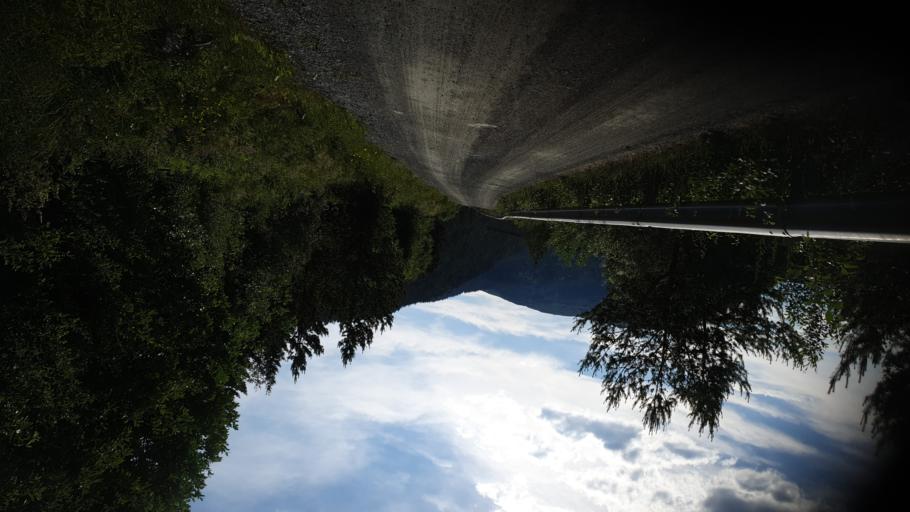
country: NO
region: Sor-Trondelag
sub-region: Trondheim
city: Trondheim
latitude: 63.5763
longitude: 10.3771
